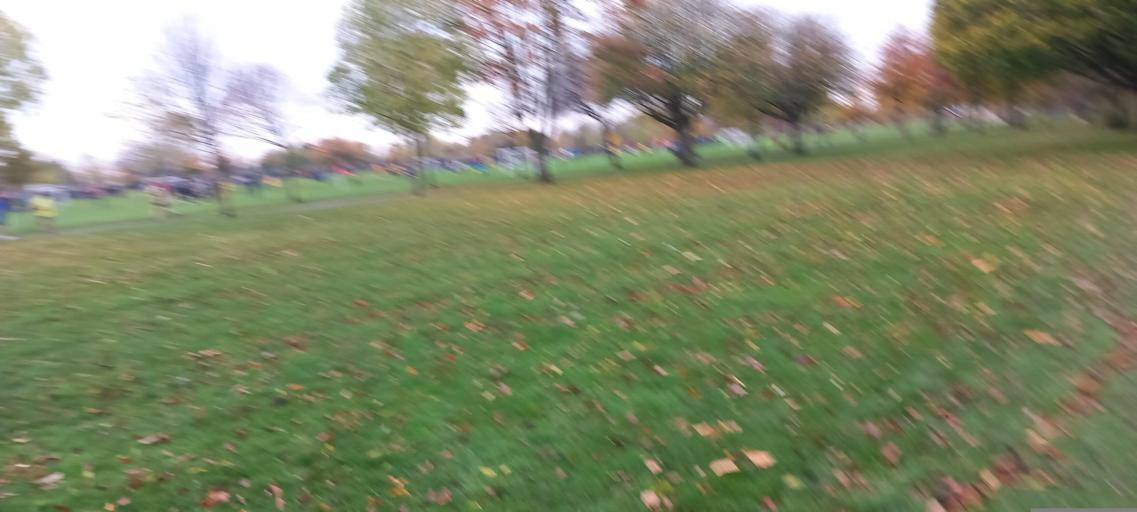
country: GB
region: England
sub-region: East Riding of Yorkshire
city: Airmyn
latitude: 53.7121
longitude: -0.8926
